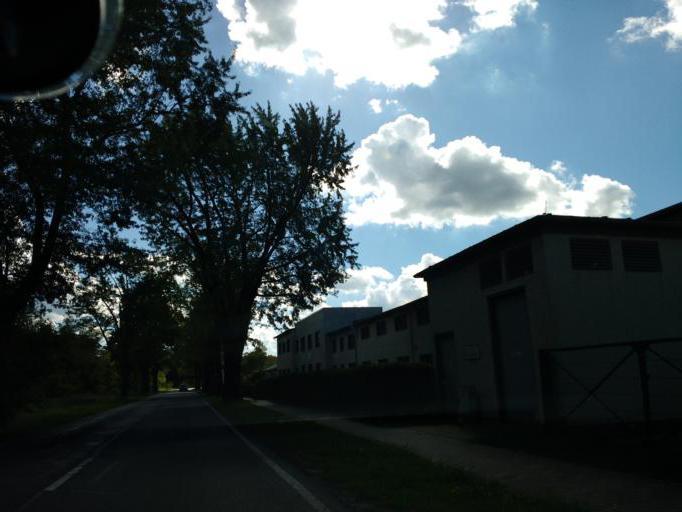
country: DE
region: Brandenburg
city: Mittenwalde
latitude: 52.2163
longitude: 13.5833
